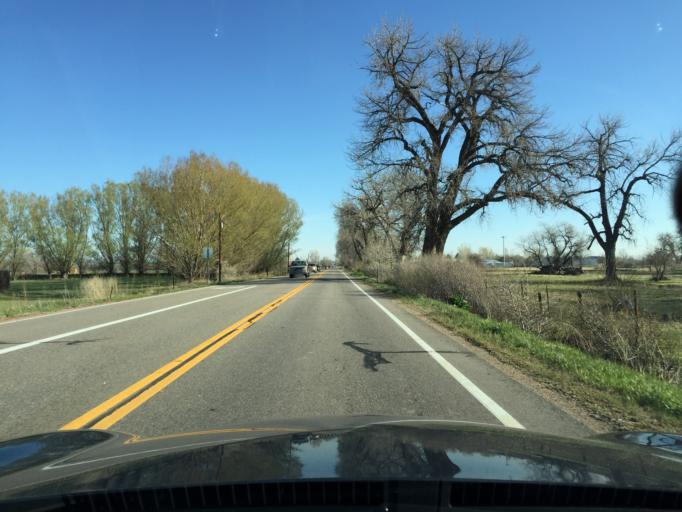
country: US
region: Colorado
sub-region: Boulder County
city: Erie
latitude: 40.0696
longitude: -105.0554
